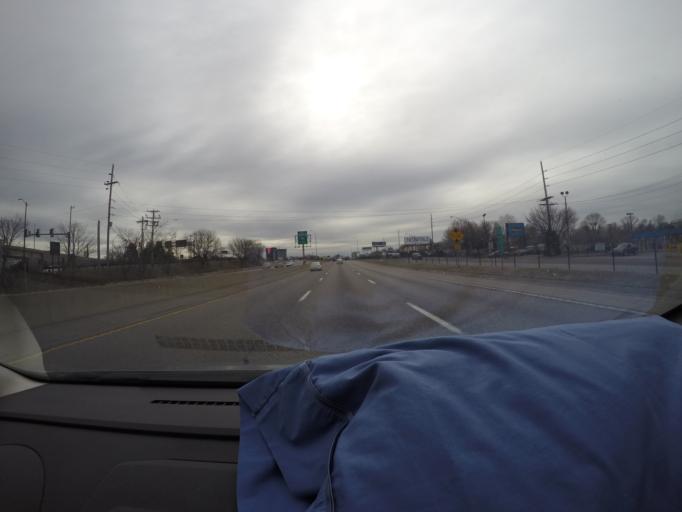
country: US
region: Missouri
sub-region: Saint Louis County
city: Woodson Terrace
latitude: 38.7348
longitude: -90.3548
